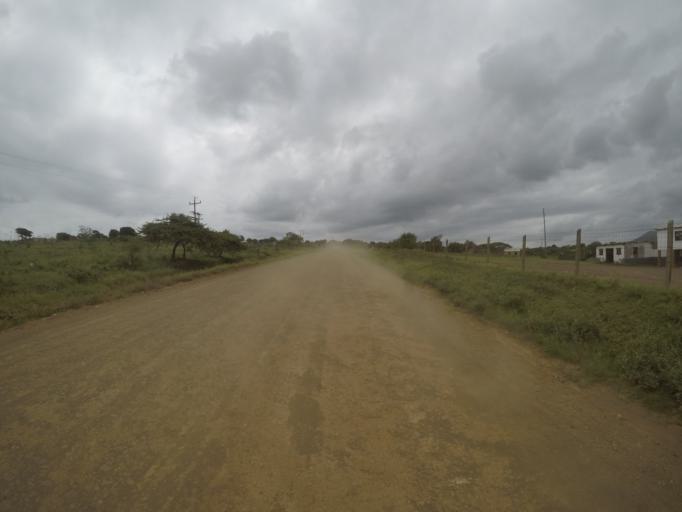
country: ZA
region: KwaZulu-Natal
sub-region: uThungulu District Municipality
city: Empangeni
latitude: -28.5847
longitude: 31.8455
